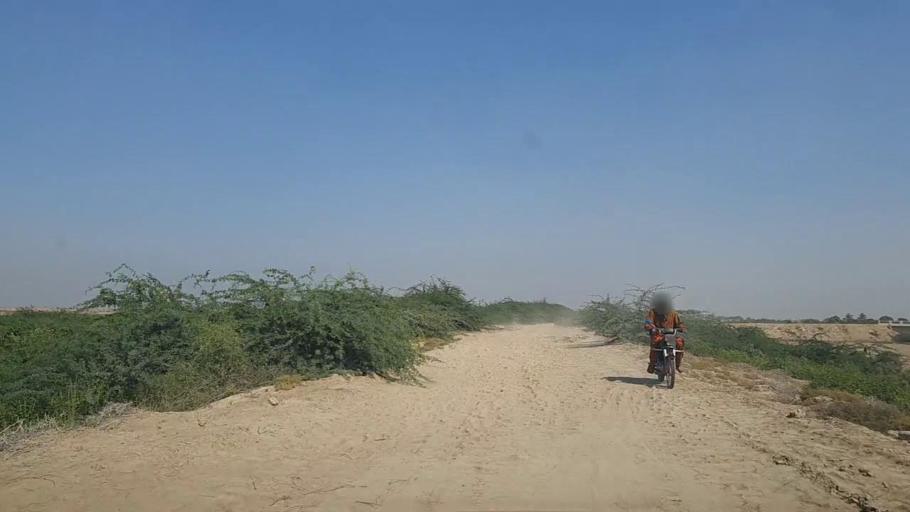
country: PK
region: Sindh
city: Thatta
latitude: 24.8477
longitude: 68.0257
